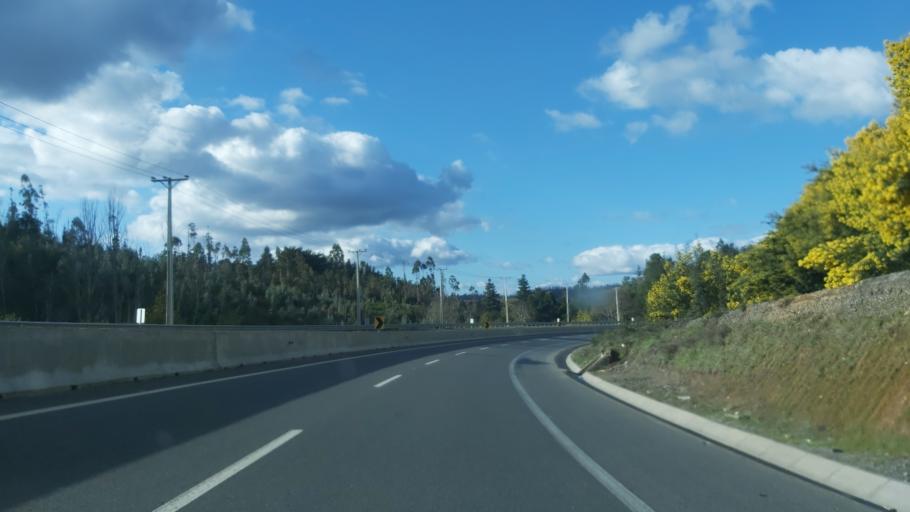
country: CL
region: Biobio
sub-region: Provincia de Concepcion
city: Penco
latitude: -36.8504
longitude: -72.9066
